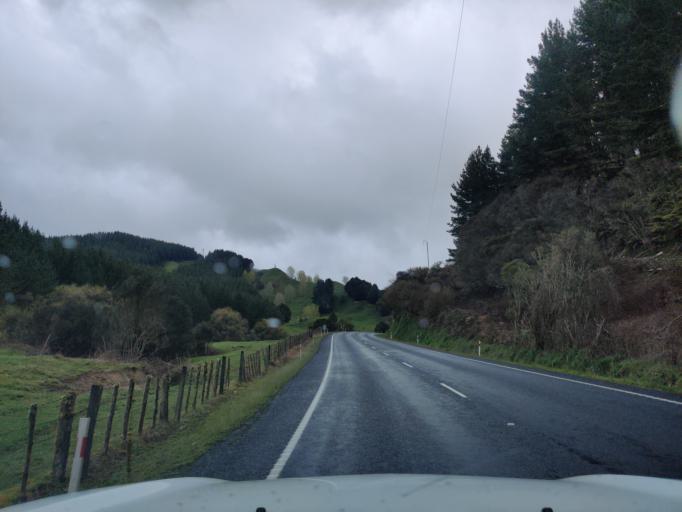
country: NZ
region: Waikato
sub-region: Otorohanga District
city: Otorohanga
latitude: -38.6627
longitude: 175.2066
